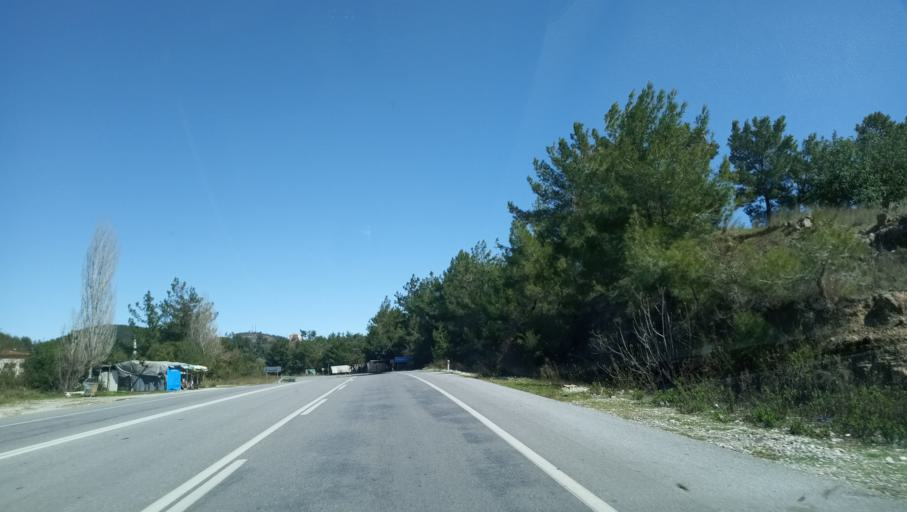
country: TR
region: Antalya
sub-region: Manavgat
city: Kizilagac
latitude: 36.7551
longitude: 31.6307
